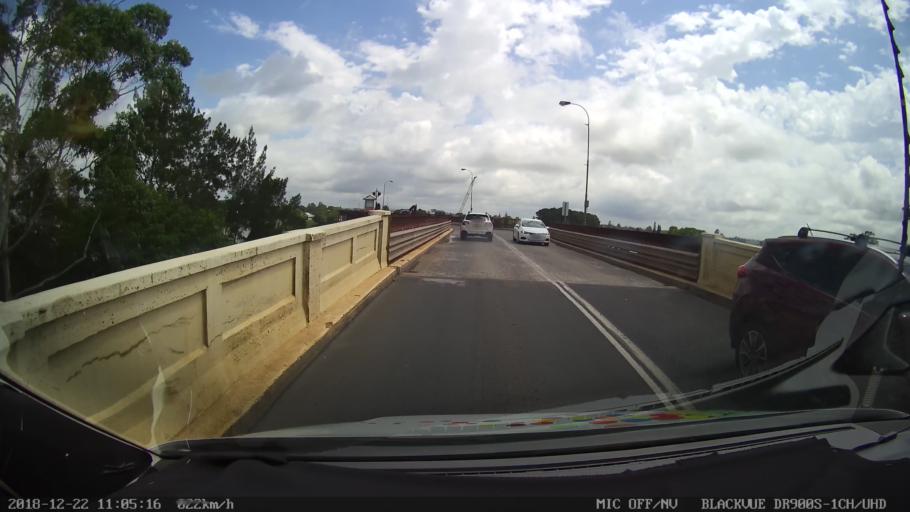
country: AU
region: New South Wales
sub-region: Clarence Valley
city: Grafton
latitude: -29.7000
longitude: 152.9425
